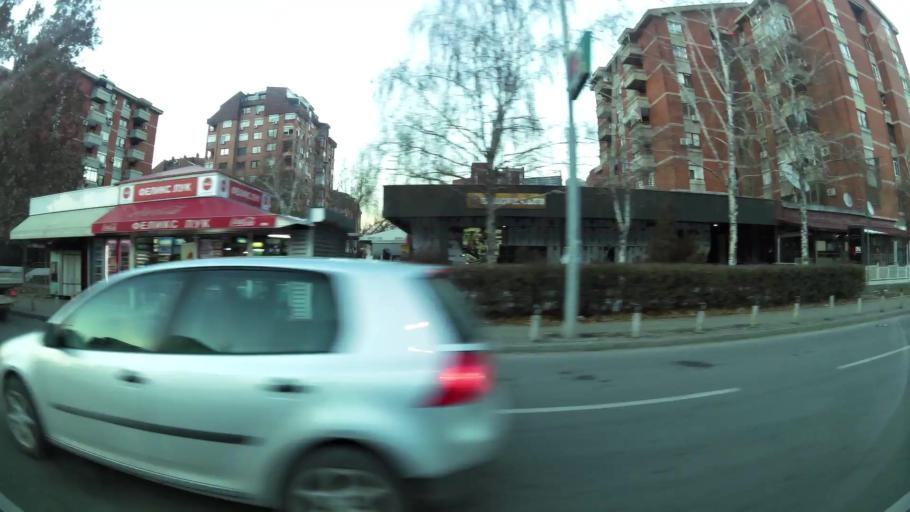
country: MK
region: Karpos
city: Skopje
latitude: 41.9958
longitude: 21.4092
